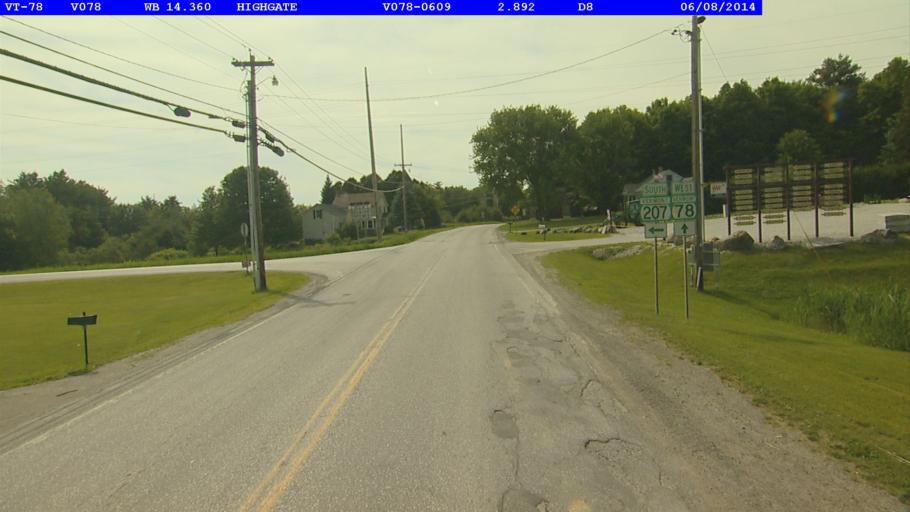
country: US
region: Vermont
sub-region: Franklin County
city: Swanton
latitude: 44.9387
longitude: -73.0488
